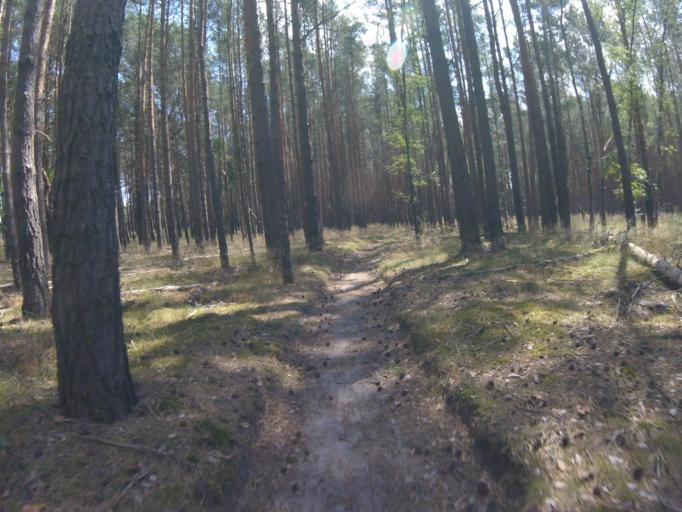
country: DE
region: Brandenburg
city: Bestensee
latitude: 52.2733
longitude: 13.6887
